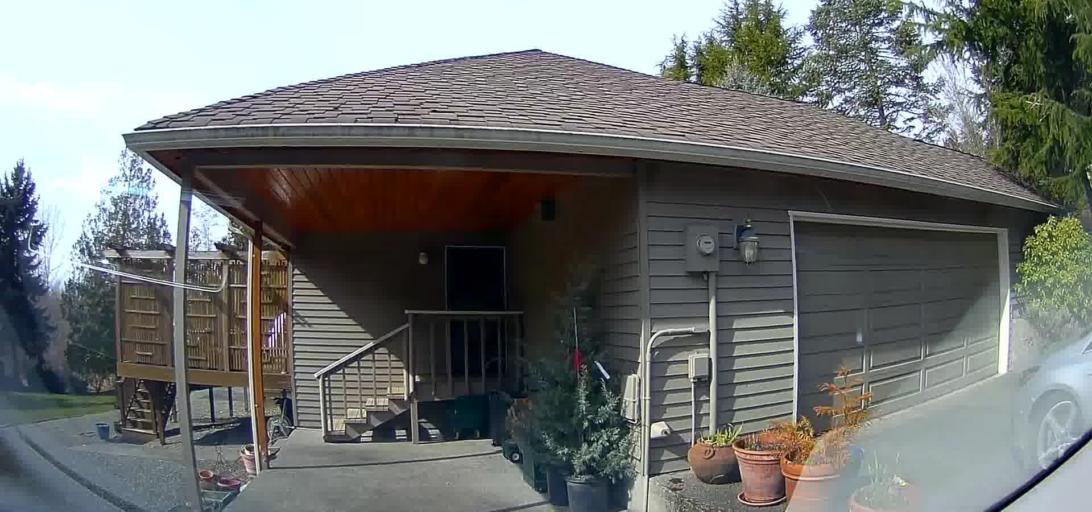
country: US
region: Washington
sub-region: Skagit County
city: Mount Vernon
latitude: 48.3914
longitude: -122.3137
